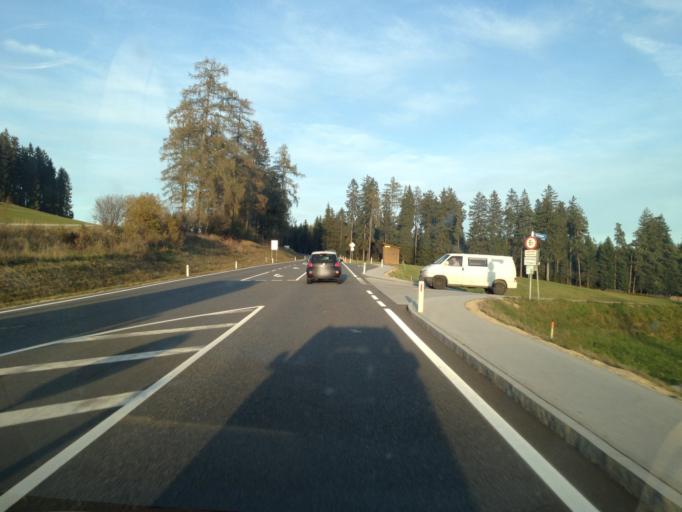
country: AT
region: Upper Austria
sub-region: Politischer Bezirk Freistadt
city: Freistadt
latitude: 48.5422
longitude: 14.6263
